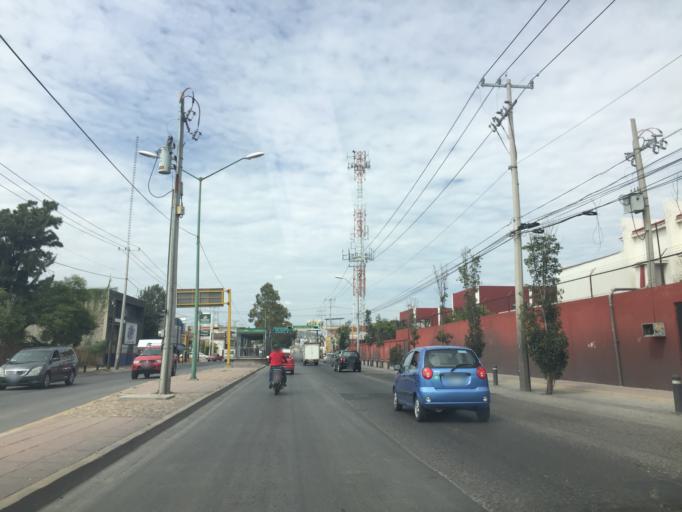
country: MX
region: Guanajuato
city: Leon
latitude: 21.1029
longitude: -101.6880
